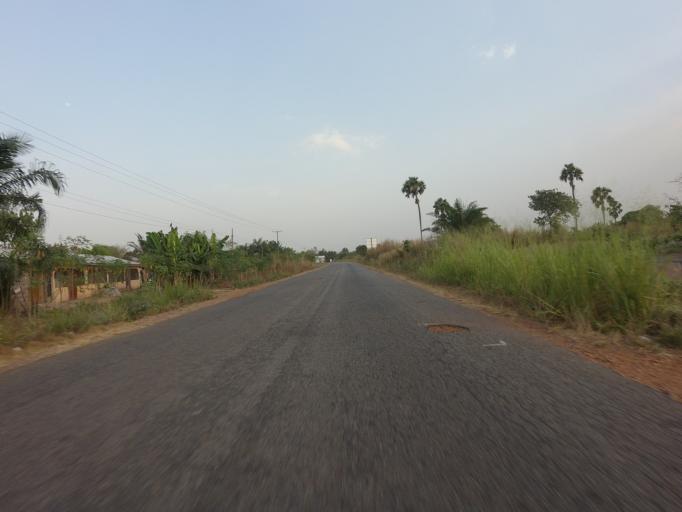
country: GH
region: Volta
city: Ho
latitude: 6.5708
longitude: 0.3891
